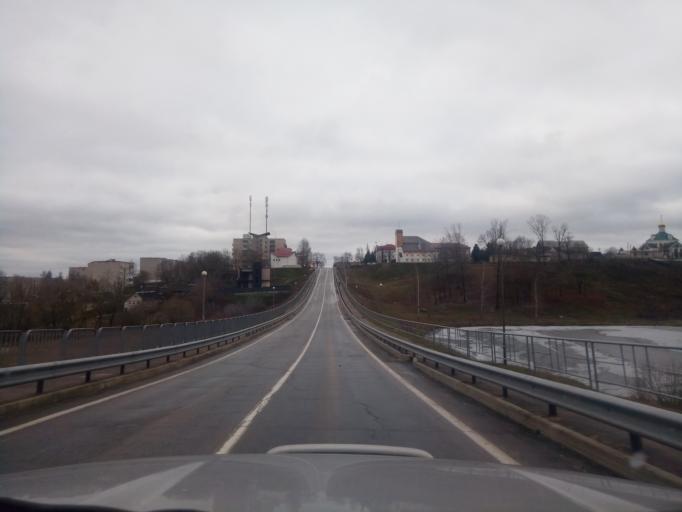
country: BY
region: Minsk
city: Kapyl'
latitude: 53.1535
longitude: 27.0961
